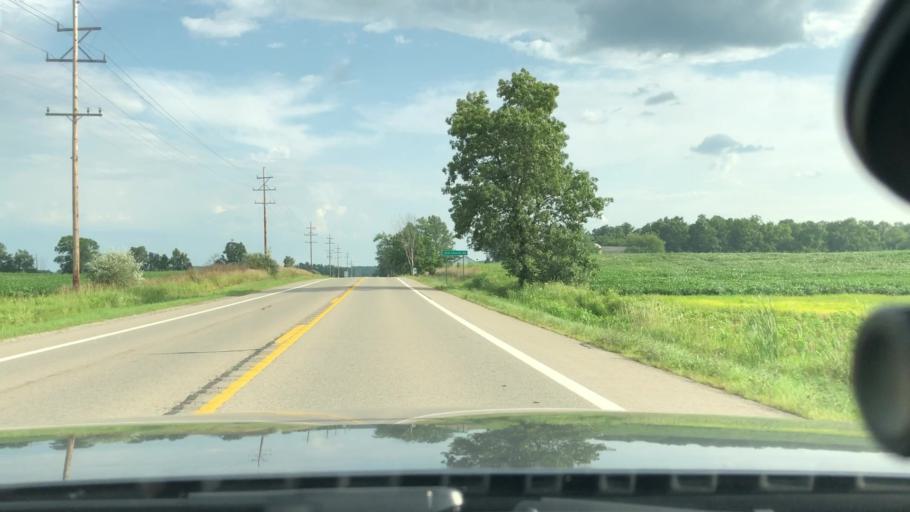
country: US
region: Michigan
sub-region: Washtenaw County
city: Chelsea
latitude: 42.2612
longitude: -84.0341
